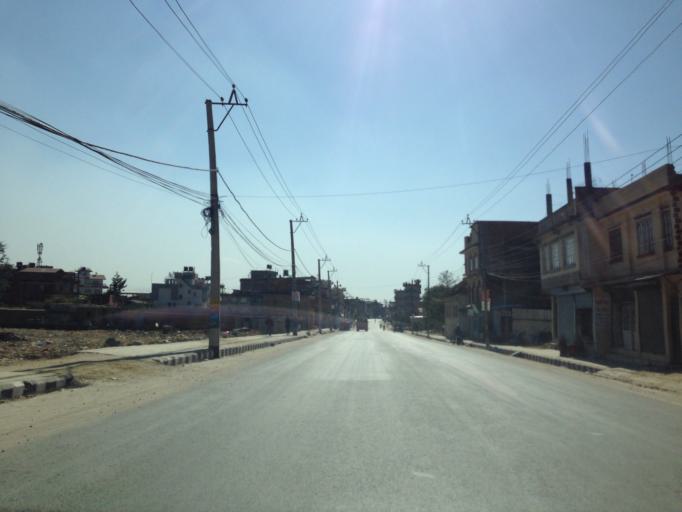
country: NP
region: Central Region
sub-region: Bagmati Zone
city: Kathmandu
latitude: 27.7633
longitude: 85.3531
